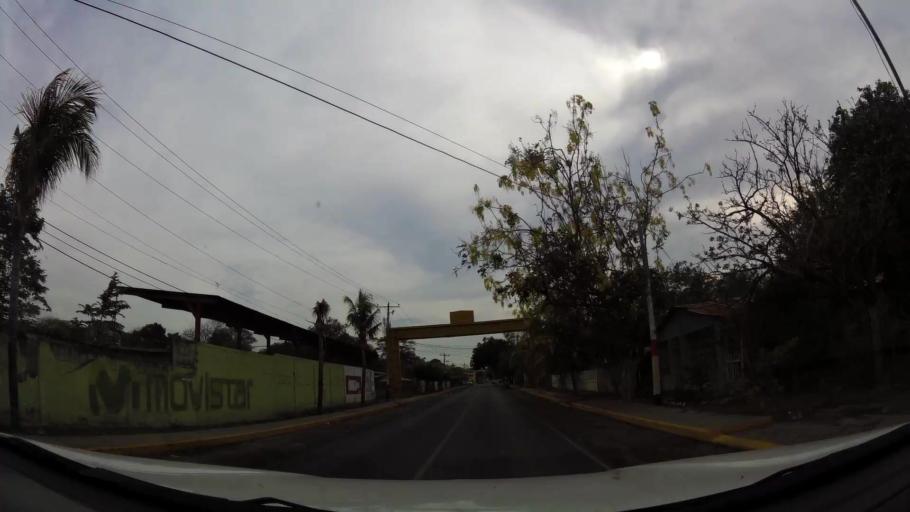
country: NI
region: Rivas
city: San Jorge
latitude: 11.4576
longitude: -85.7966
